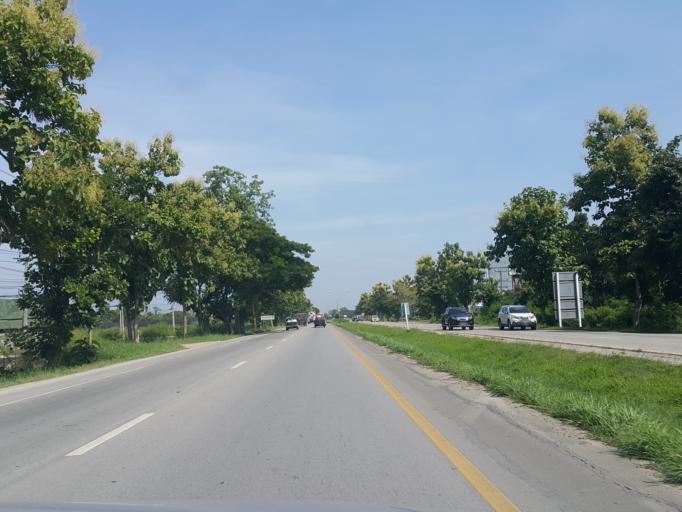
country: TH
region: Chiang Mai
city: Saraphi
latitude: 18.7228
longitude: 99.0412
